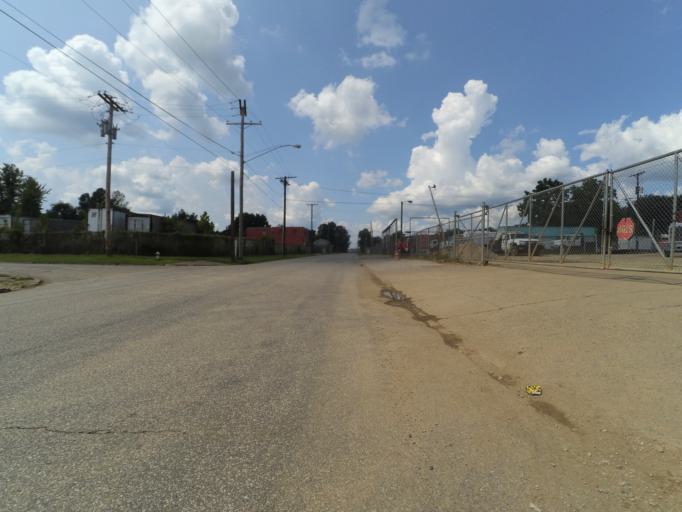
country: US
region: West Virginia
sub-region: Cabell County
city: Huntington
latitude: 38.4173
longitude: -82.4675
